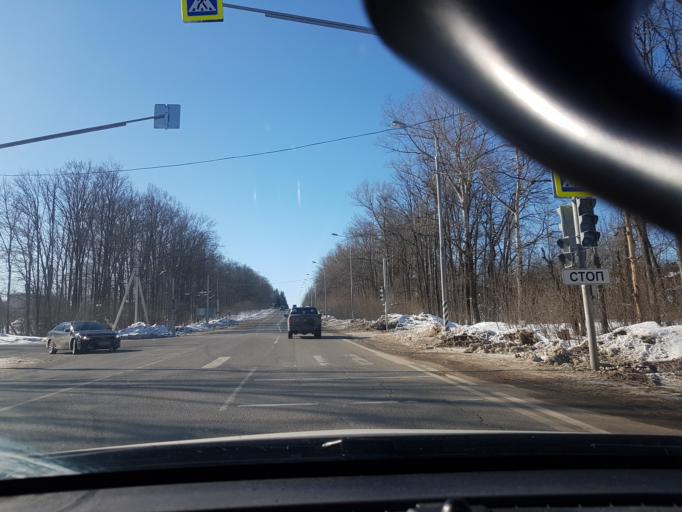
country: RU
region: Moskovskaya
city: Kostrovo
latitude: 55.9122
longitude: 36.7557
